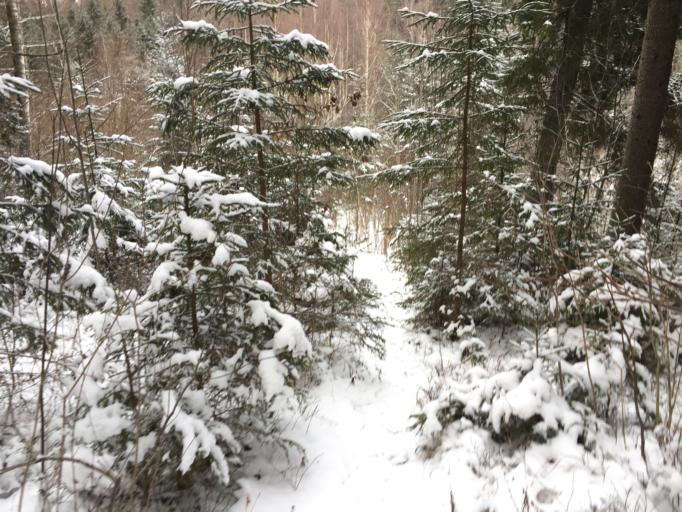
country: LV
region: Amatas Novads
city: Drabesi
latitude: 57.2247
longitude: 25.1701
